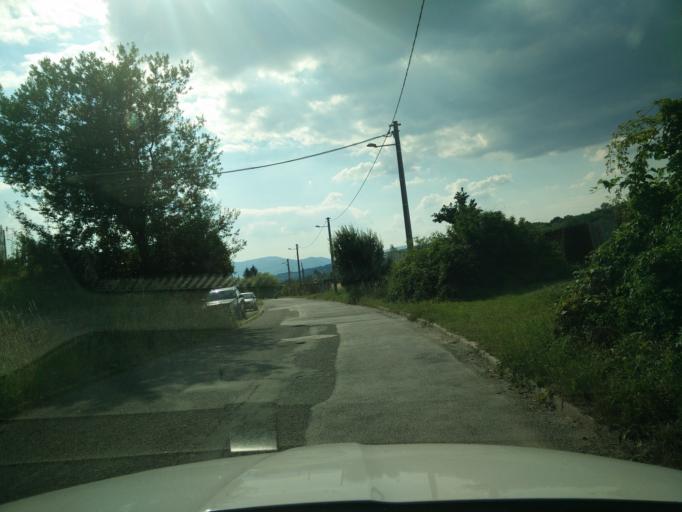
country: SK
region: Nitriansky
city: Prievidza
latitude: 48.7682
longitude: 18.6418
